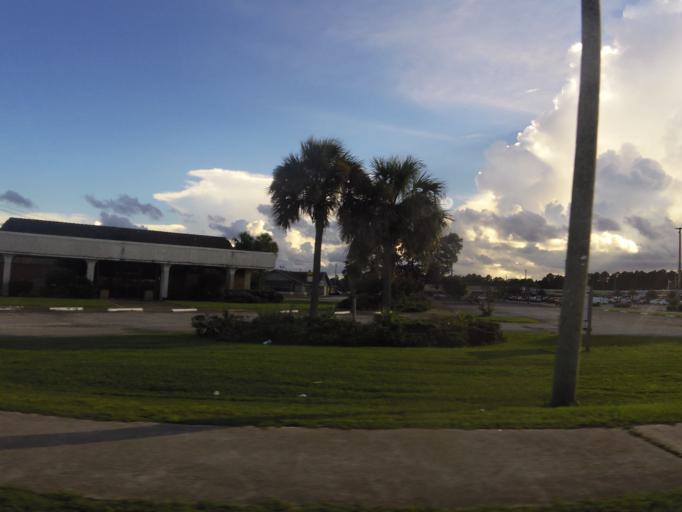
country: US
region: Georgia
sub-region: Camden County
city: St Marys
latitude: 30.7514
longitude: -81.5754
